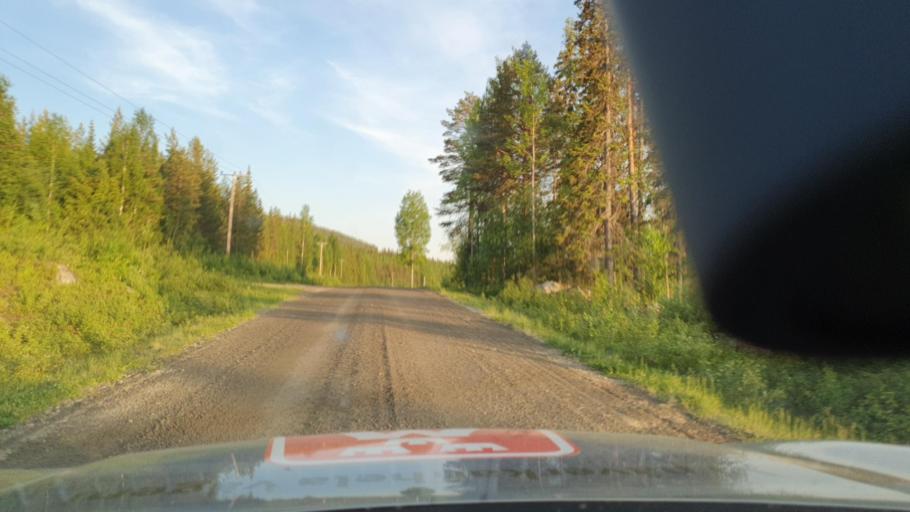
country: SE
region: Norrbotten
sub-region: Bodens Kommun
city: Boden
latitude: 66.1365
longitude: 21.5634
